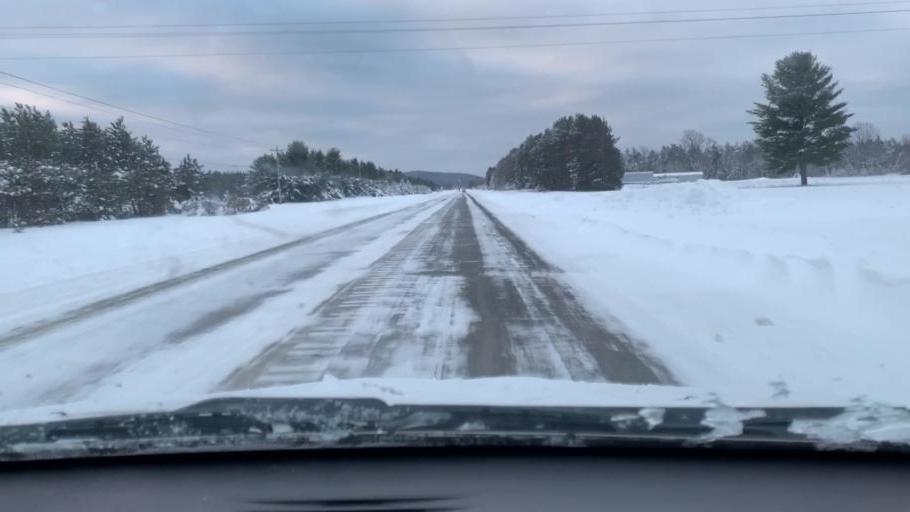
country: US
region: Michigan
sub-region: Antrim County
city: Mancelona
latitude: 44.9270
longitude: -85.0509
